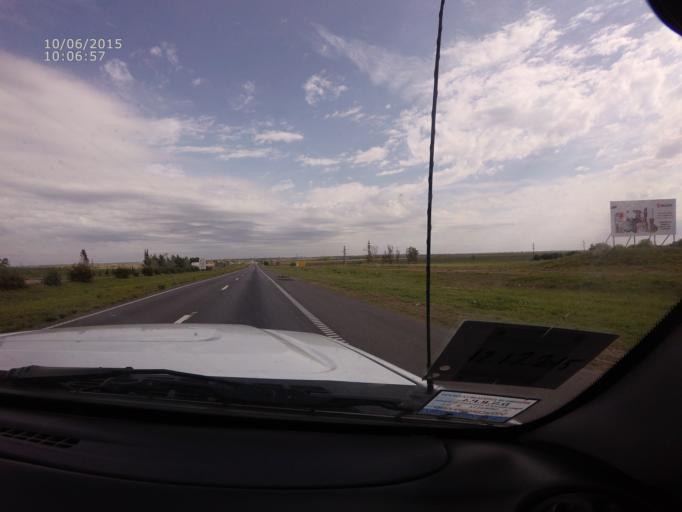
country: AR
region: Buenos Aires
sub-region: Partido de Baradero
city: Baradero
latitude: -33.8235
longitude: -59.5850
